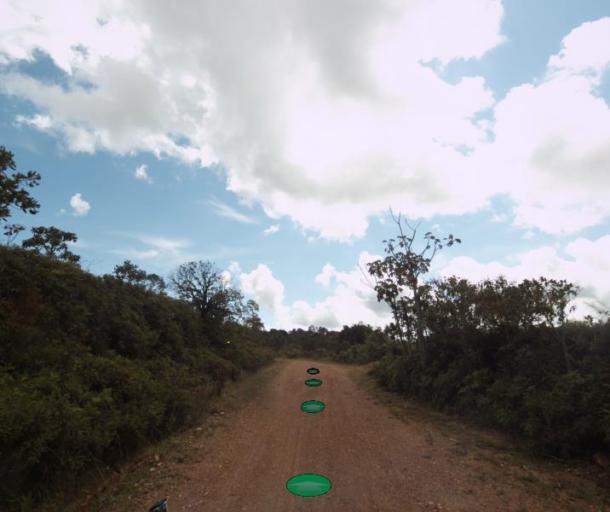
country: BR
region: Goias
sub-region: Pirenopolis
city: Pirenopolis
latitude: -15.7905
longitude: -48.9102
